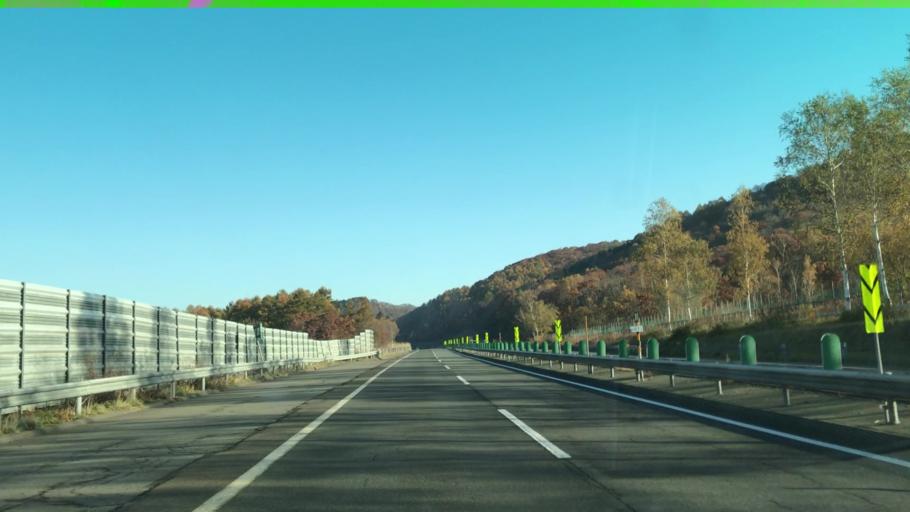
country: JP
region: Hokkaido
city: Sunagawa
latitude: 43.4061
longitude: 141.9059
